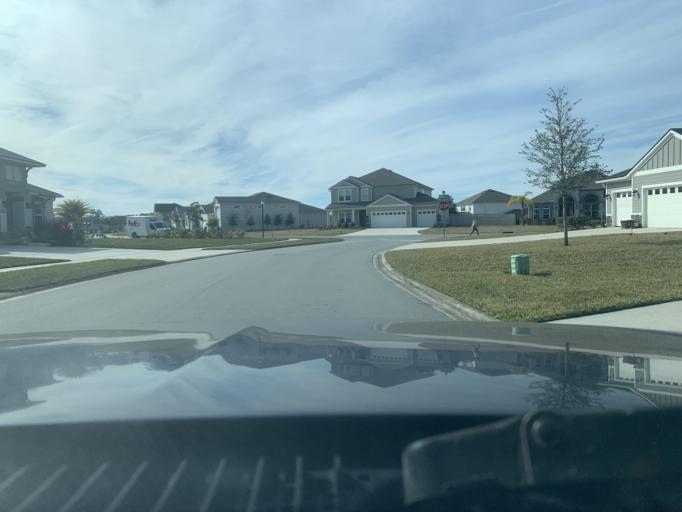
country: US
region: Florida
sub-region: Clay County
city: Green Cove Springs
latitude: 29.9814
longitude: -81.5239
